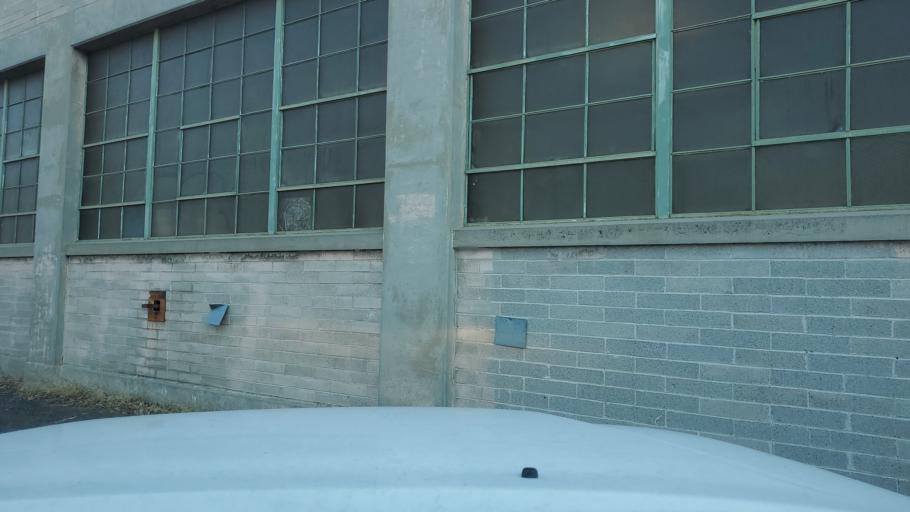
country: US
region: Utah
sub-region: Salt Lake County
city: Salt Lake City
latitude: 40.7405
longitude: -111.8951
